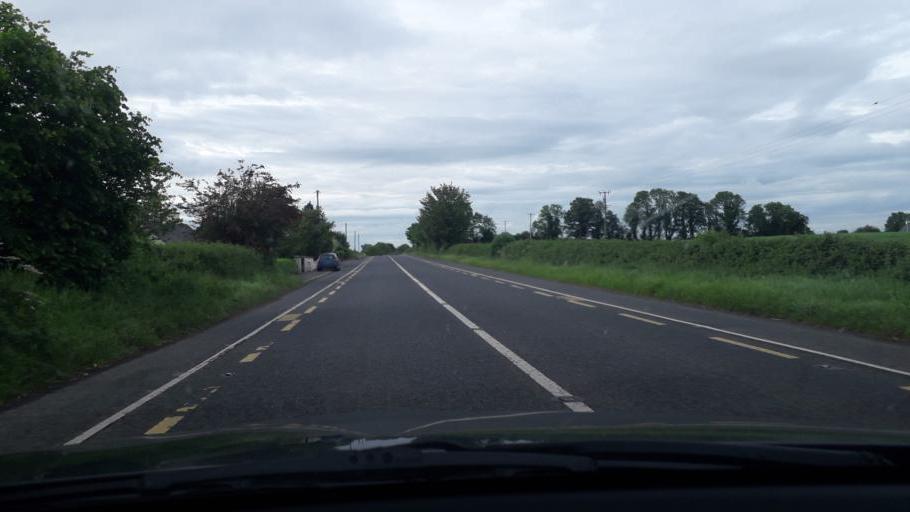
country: IE
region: Leinster
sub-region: County Carlow
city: Carlow
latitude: 52.8052
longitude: -6.9528
